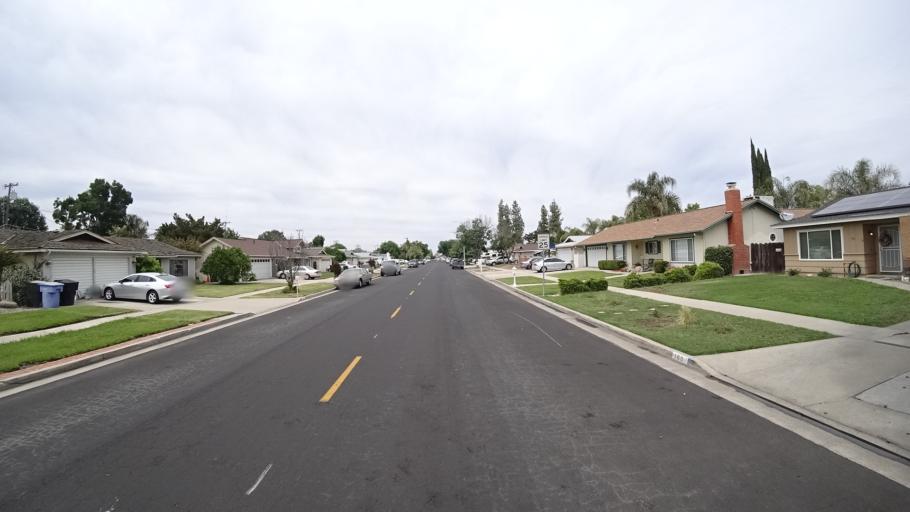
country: US
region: California
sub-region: Kings County
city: Hanford
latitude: 36.3540
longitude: -119.6476
